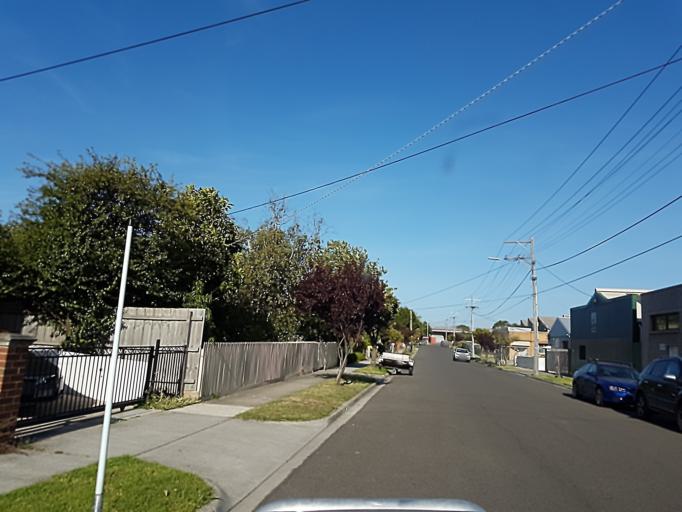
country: AU
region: Victoria
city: Clayton
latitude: -37.9089
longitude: 145.1074
